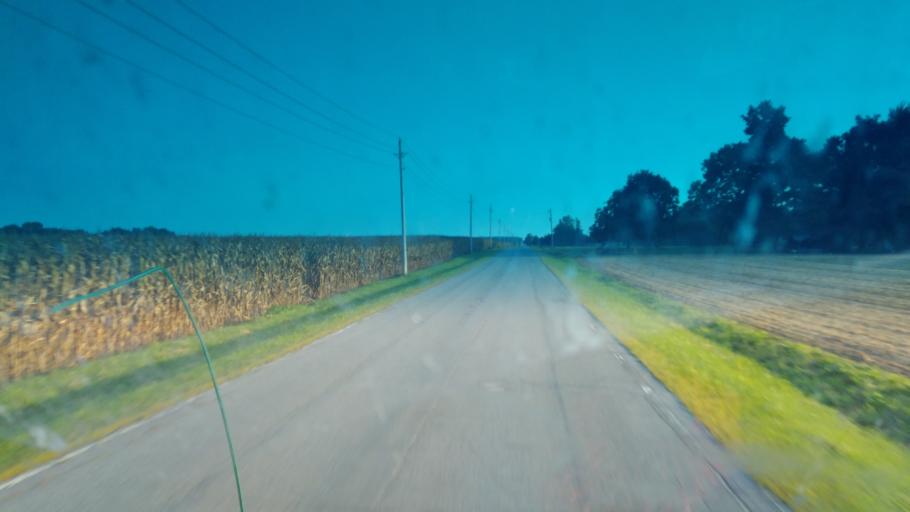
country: US
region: Ohio
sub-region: Crawford County
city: Galion
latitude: 40.8151
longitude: -82.8188
